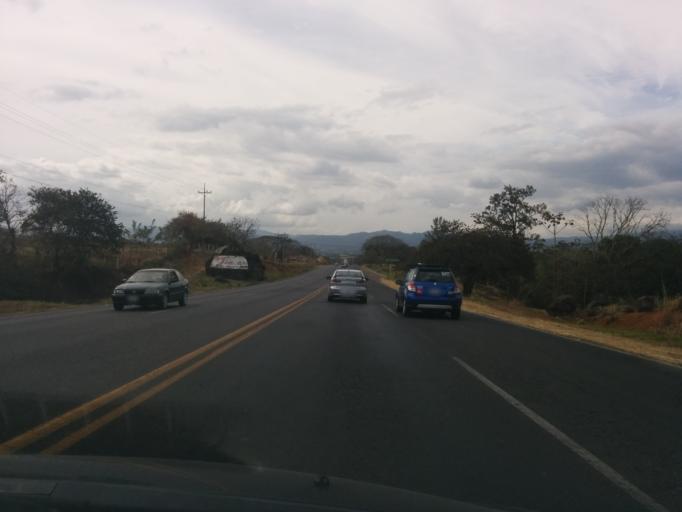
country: CR
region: Alajuela
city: Carrillos
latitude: 9.9996
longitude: -84.2795
